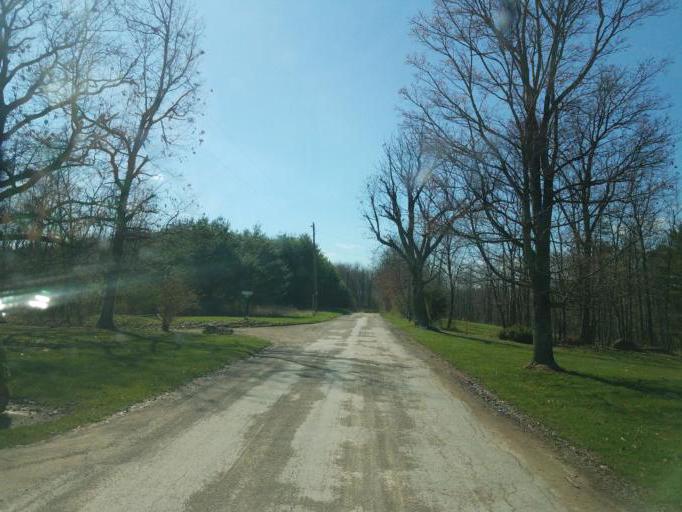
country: US
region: Ohio
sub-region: Knox County
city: Oak Hill
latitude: 40.3953
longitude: -82.2062
